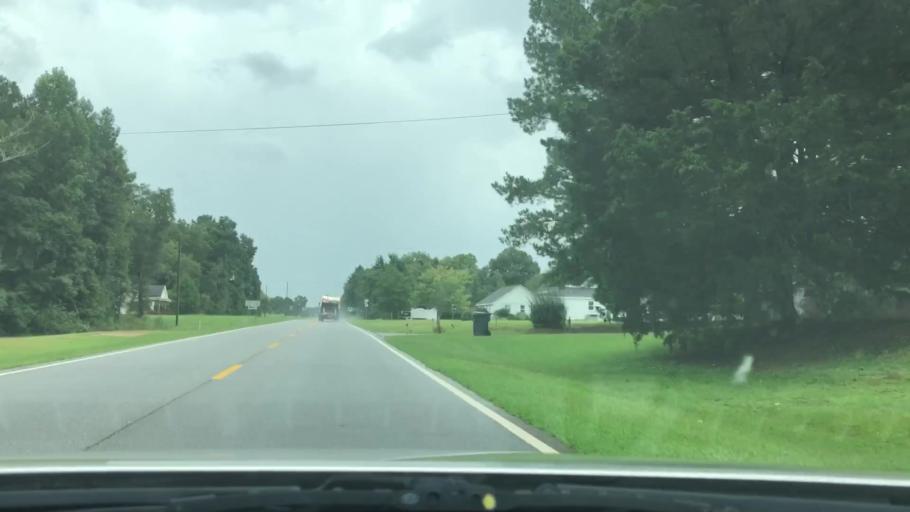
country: US
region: Georgia
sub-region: Lamar County
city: Barnesville
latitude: 33.0731
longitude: -84.2428
